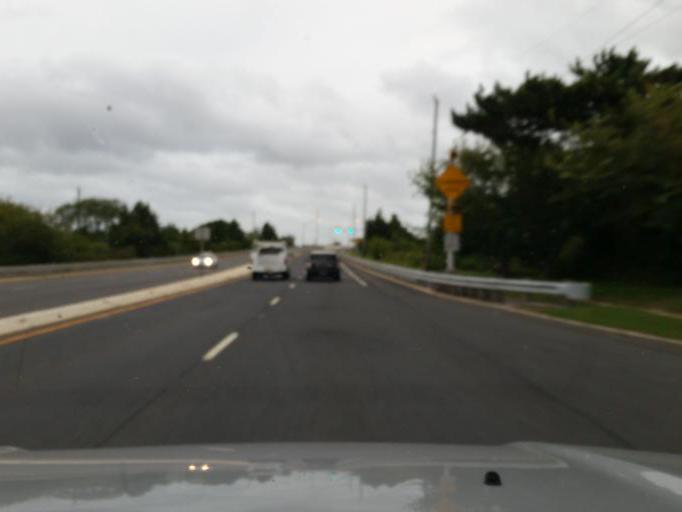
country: US
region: New Jersey
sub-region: Cape May County
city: Wildwood Crest
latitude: 38.9923
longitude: -74.8370
